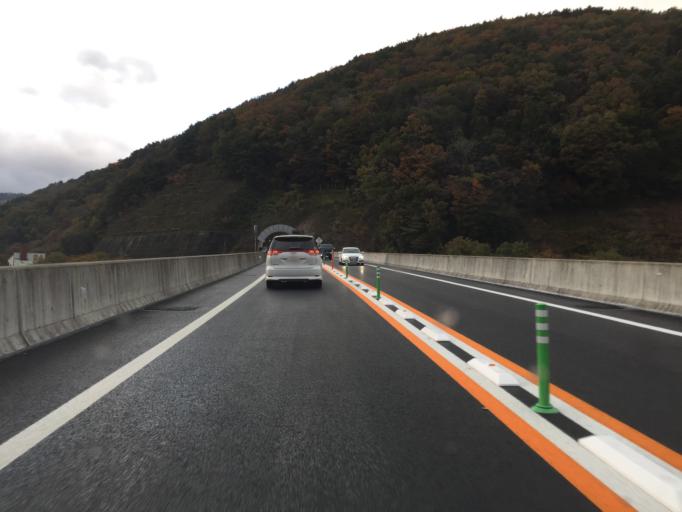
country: JP
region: Fukushima
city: Fukushima-shi
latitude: 37.8282
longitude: 140.3998
